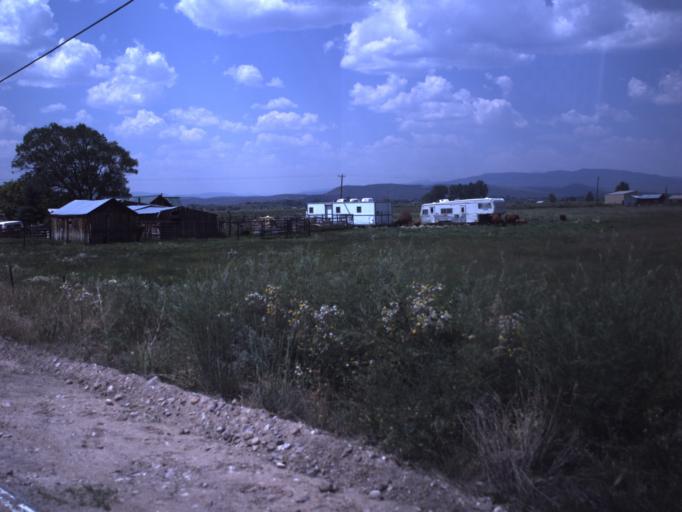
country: US
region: Utah
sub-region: Duchesne County
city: Roosevelt
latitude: 40.4330
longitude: -110.0189
